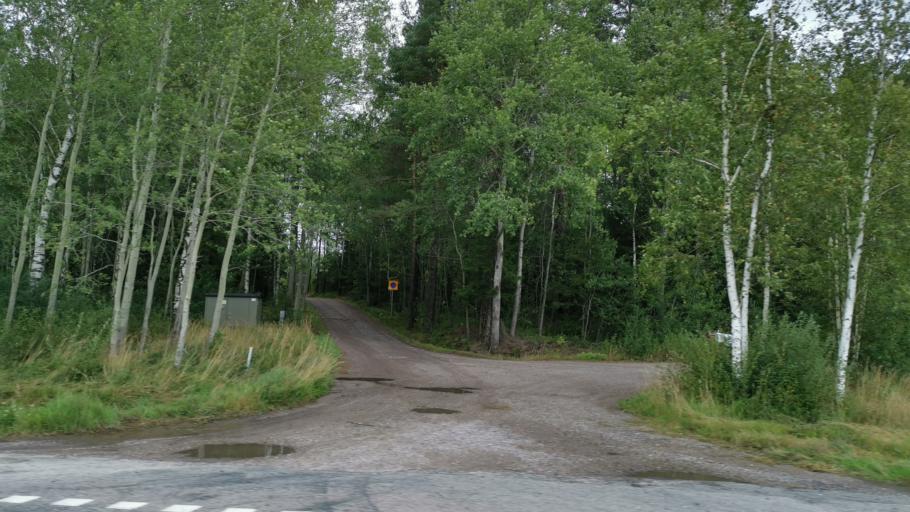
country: SE
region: Vaestra Goetaland
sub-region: Trollhattan
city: Sjuntorp
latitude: 58.3378
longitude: 12.1233
